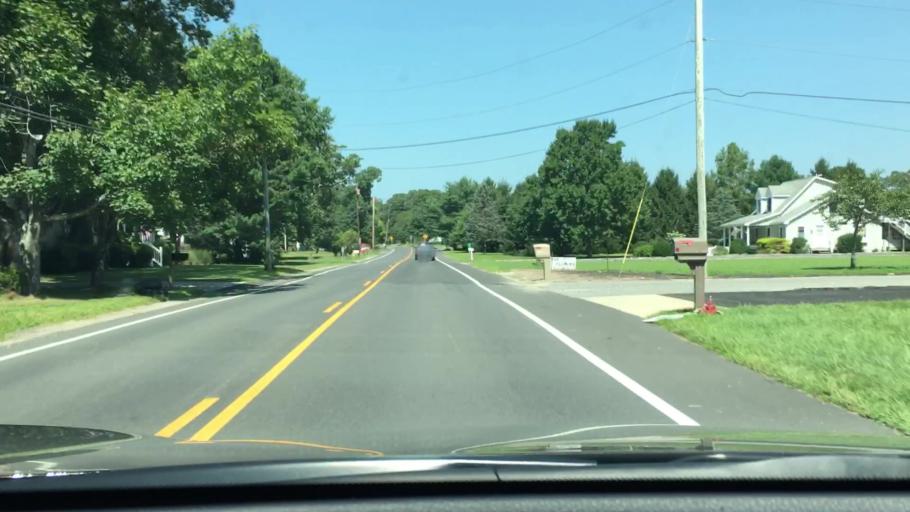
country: US
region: New Jersey
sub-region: Cape May County
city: Woodbine
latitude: 39.2661
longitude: -74.8637
